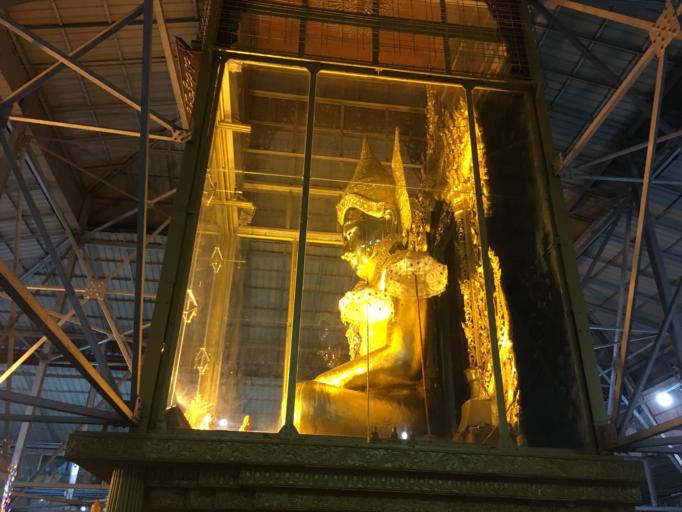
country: MM
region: Mon
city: Mawlamyine
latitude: 16.4787
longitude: 97.6295
